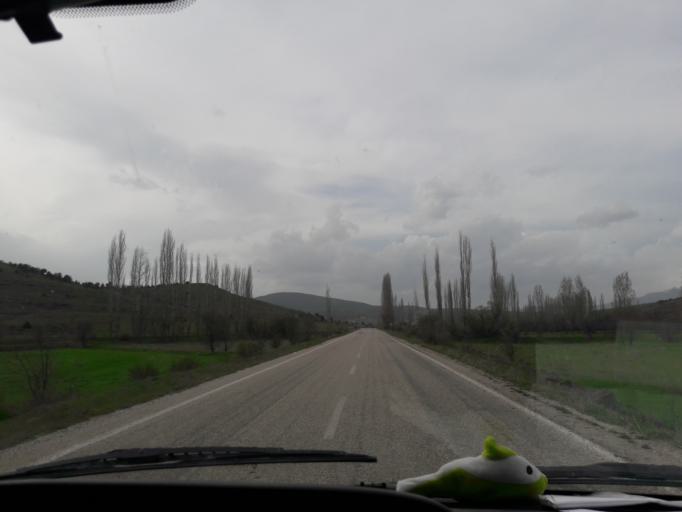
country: TR
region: Gumushane
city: Siran
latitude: 40.1659
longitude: 39.0064
